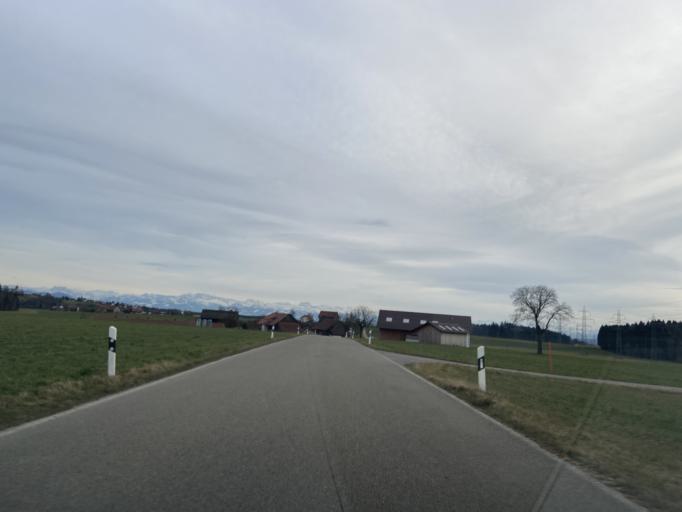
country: CH
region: Zurich
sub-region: Bezirk Winterthur
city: Brutten
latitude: 47.4864
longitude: 8.6576
